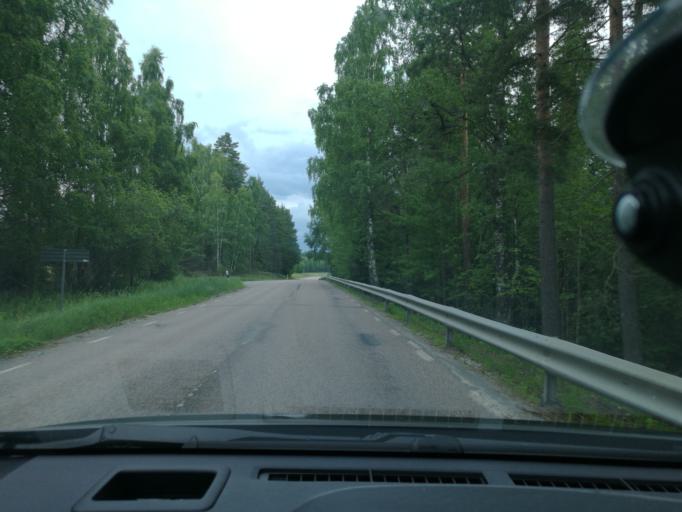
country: SE
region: Vaestmanland
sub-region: Vasteras
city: Skultuna
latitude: 59.9106
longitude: 16.3558
